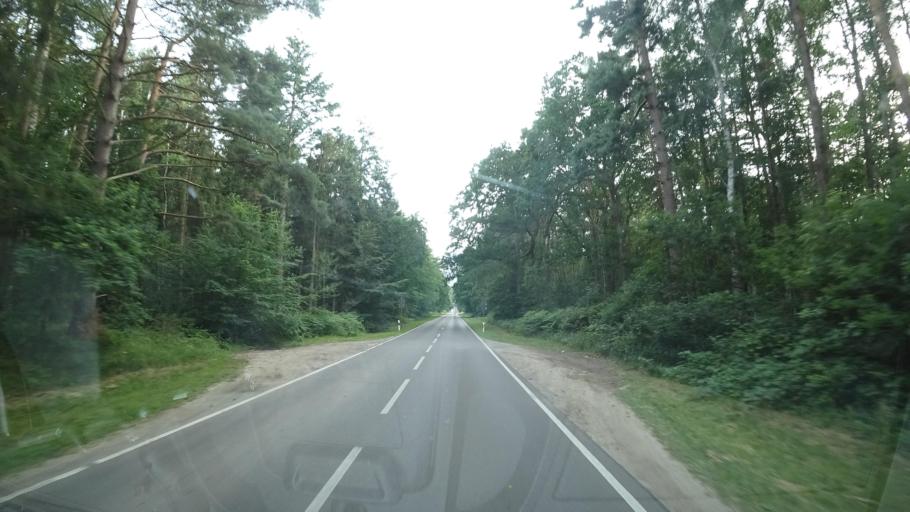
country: DE
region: Mecklenburg-Vorpommern
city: Ostseebad Binz
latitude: 54.4400
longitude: 13.5648
